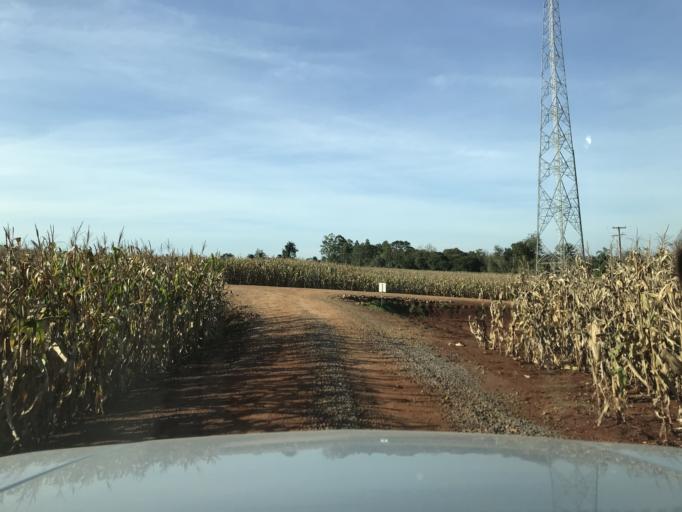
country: BR
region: Parana
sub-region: Palotina
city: Palotina
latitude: -24.2468
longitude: -53.7441
